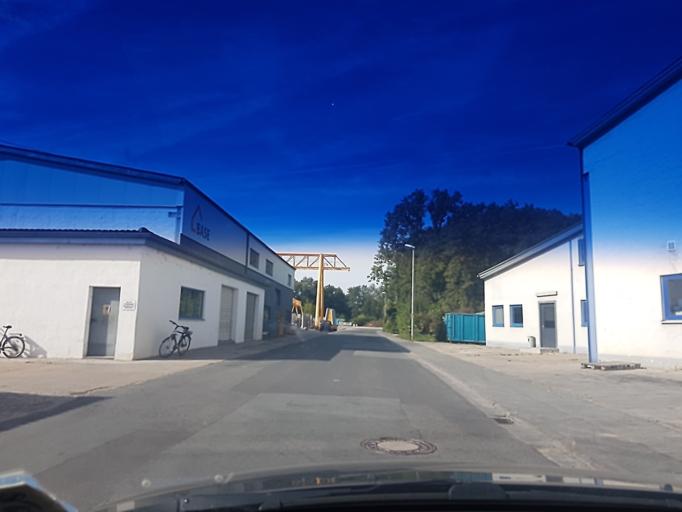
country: DE
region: Bavaria
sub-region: Upper Franconia
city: Schlusselfeld
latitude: 49.7605
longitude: 10.6140
